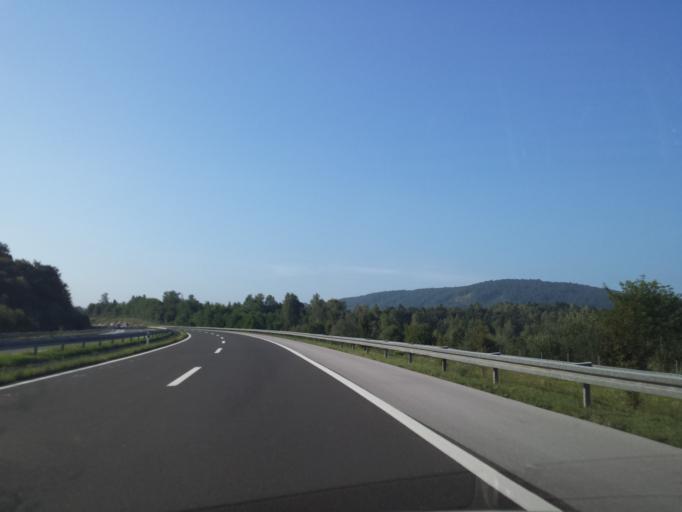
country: HR
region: Karlovacka
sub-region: Grad Ogulin
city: Ogulin
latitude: 45.3948
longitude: 15.2587
